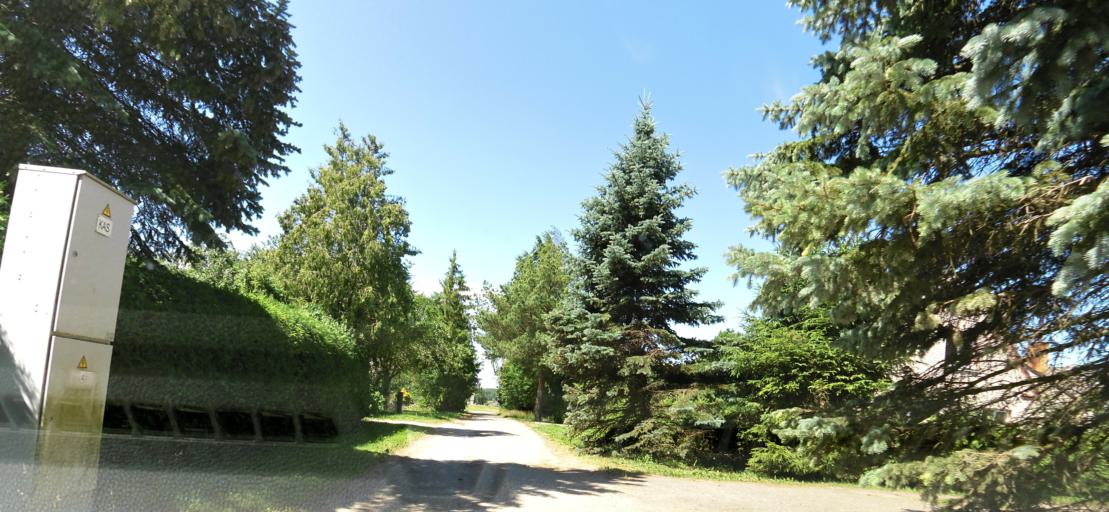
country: LT
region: Panevezys
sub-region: Birzai
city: Birzai
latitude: 56.2522
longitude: 24.5413
